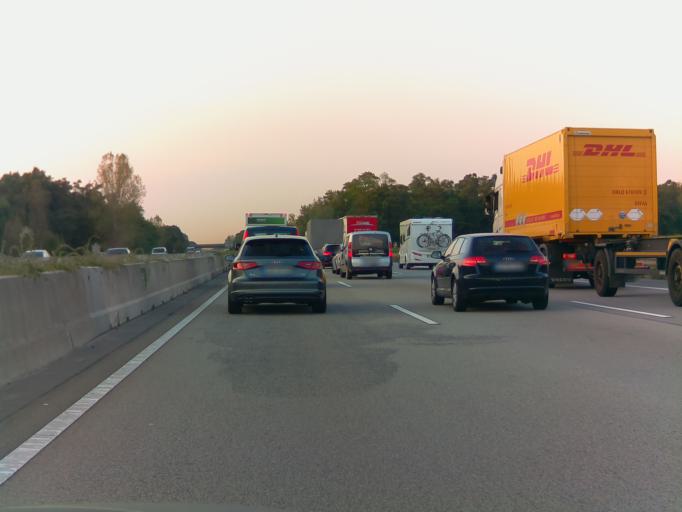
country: DE
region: Hesse
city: Viernheim
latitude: 49.5909
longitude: 8.5608
